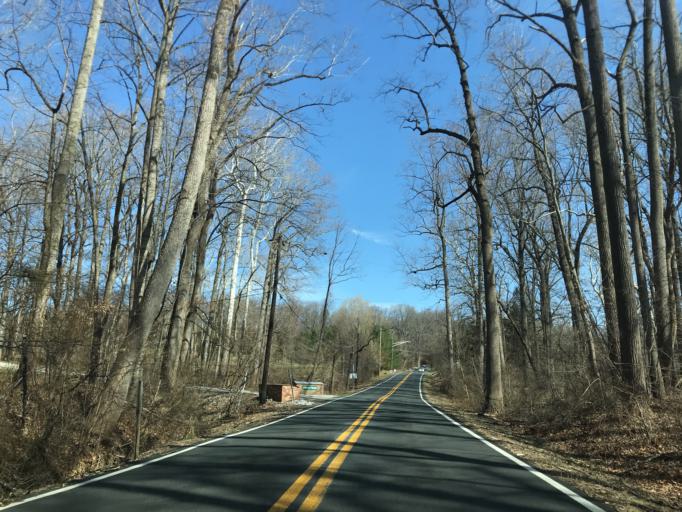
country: US
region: Maryland
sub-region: Howard County
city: Highland
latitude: 39.1527
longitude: -76.9558
